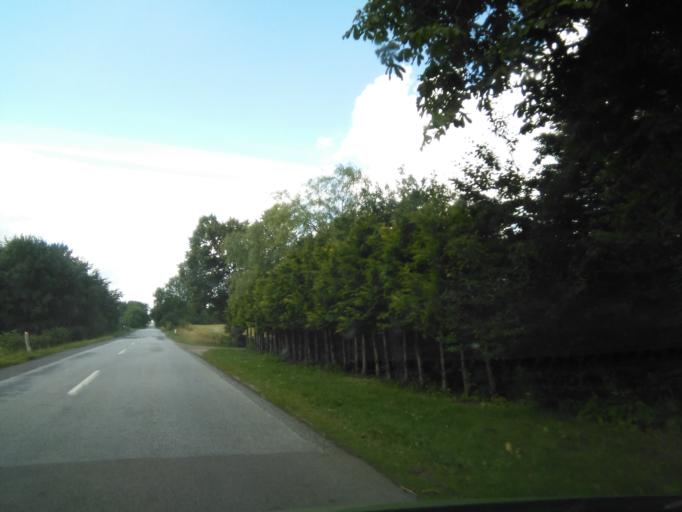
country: DK
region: Central Jutland
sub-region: Arhus Kommune
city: Tranbjerg
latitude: 56.0768
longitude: 10.1144
